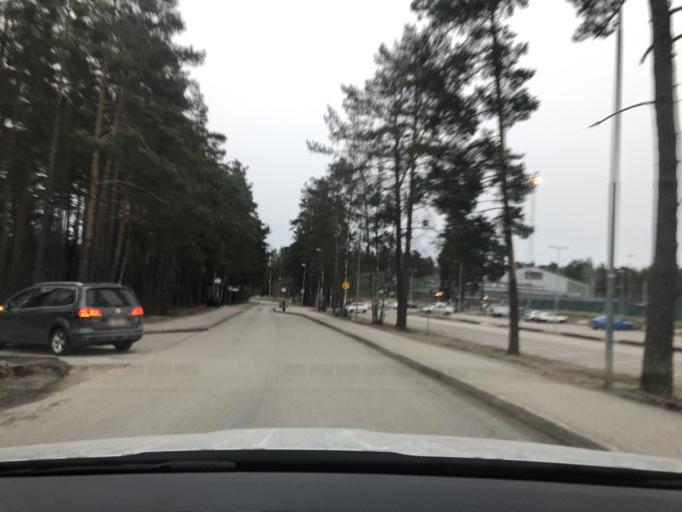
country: SE
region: Stockholm
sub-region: Botkyrka Kommun
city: Tullinge
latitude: 59.1935
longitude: 17.9023
